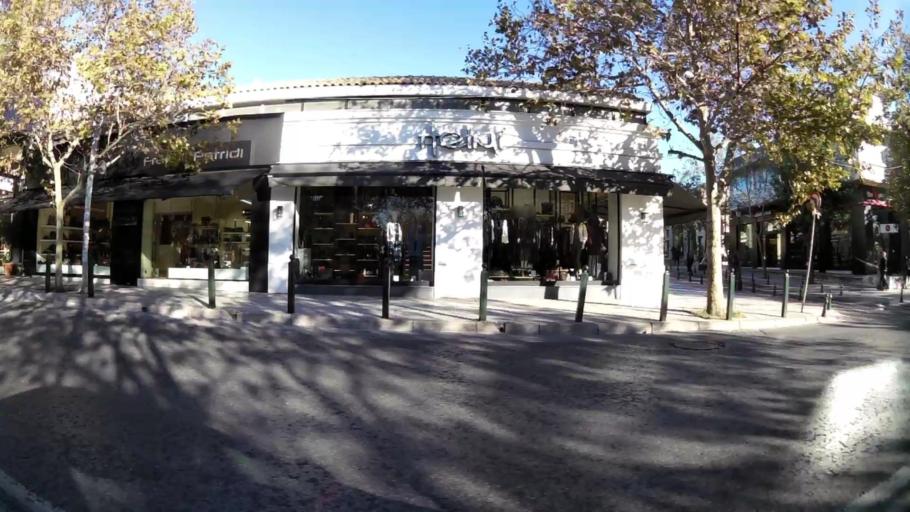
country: GR
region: Attica
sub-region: Nomarchia Athinas
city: Kifisia
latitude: 38.0734
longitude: 23.8125
